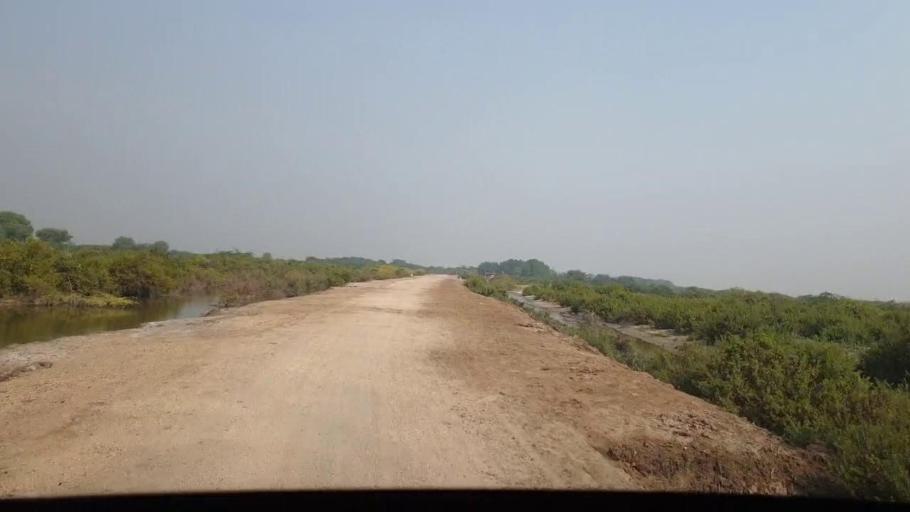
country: PK
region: Sindh
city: Jati
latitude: 24.4343
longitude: 68.4365
